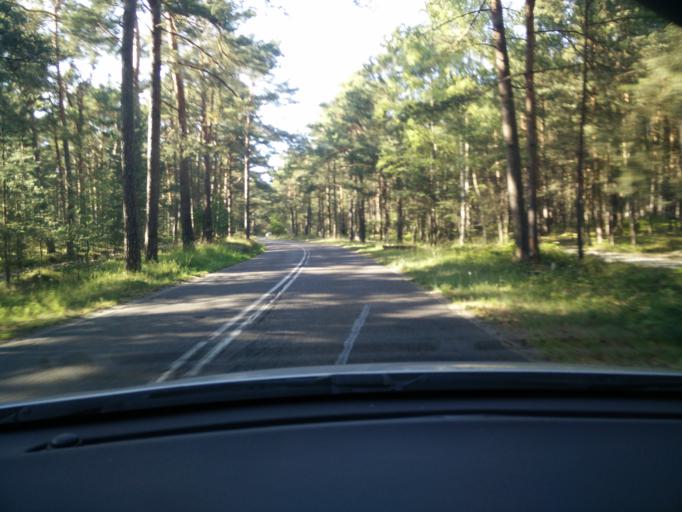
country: PL
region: Pomeranian Voivodeship
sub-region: Powiat pucki
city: Hel
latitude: 54.6405
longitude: 18.7743
